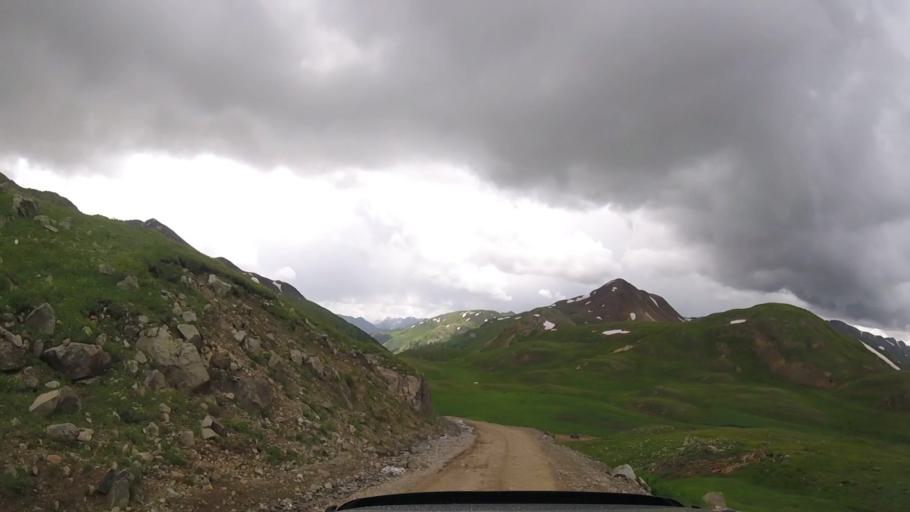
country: US
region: Colorado
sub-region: Ouray County
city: Ouray
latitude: 37.9590
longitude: -107.5757
